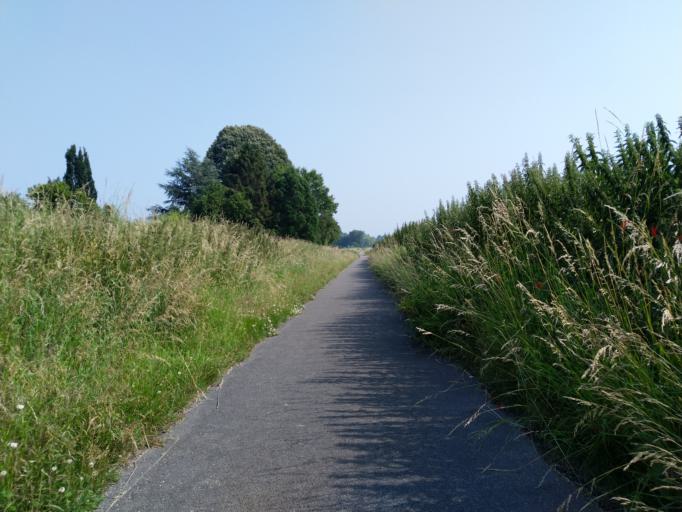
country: BE
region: Wallonia
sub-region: Province du Hainaut
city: Soignies
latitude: 50.5575
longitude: 4.0045
